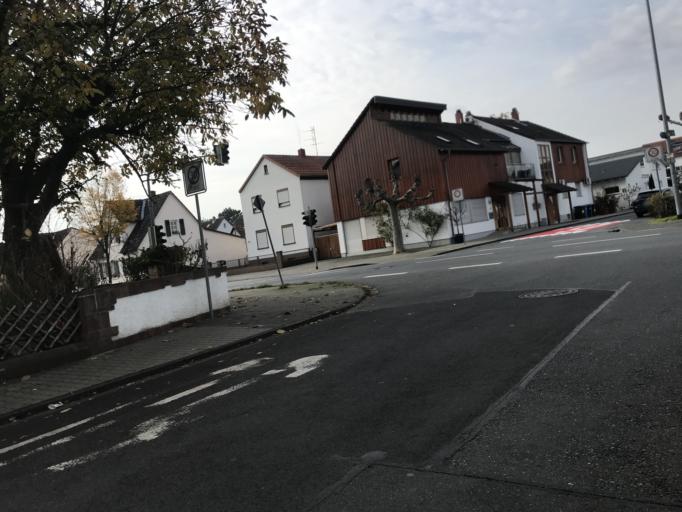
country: DE
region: Hesse
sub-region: Regierungsbezirk Darmstadt
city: Trebur
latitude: 49.9288
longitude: 8.4062
